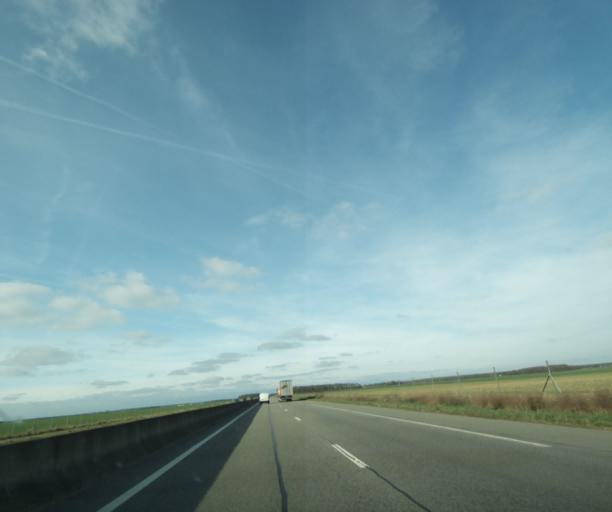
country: FR
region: Ile-de-France
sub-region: Departement des Yvelines
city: Sonchamp
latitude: 48.5930
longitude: 1.8320
